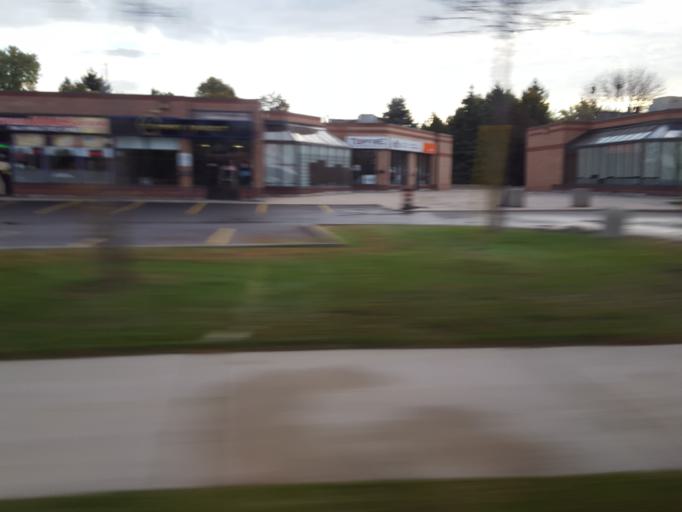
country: CA
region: Ontario
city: Newmarket
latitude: 44.0056
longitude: -79.4689
